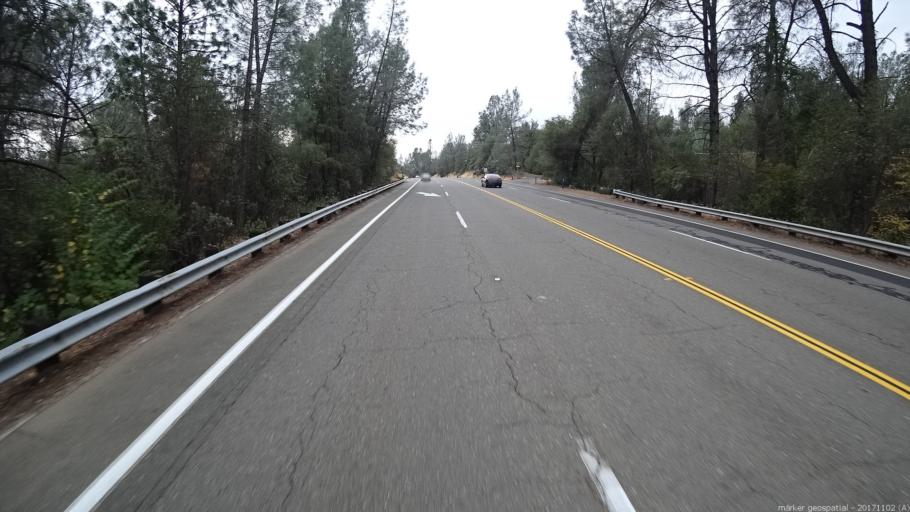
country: US
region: California
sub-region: Shasta County
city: Central Valley (historical)
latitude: 40.6609
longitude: -122.3966
